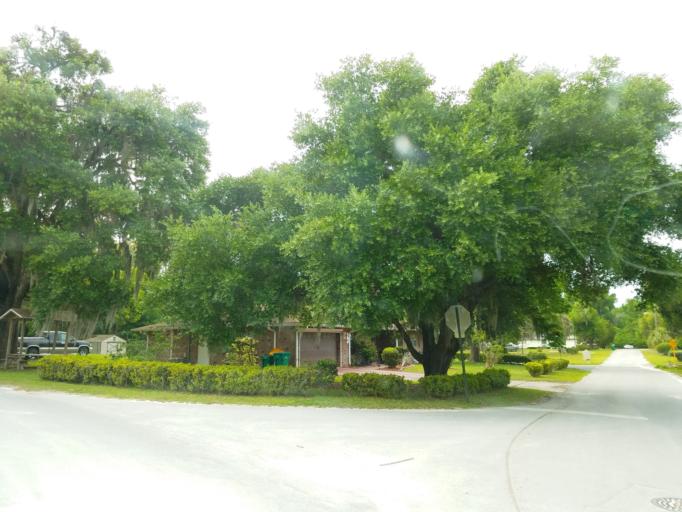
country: US
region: Florida
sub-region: Citrus County
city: Inverness
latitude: 28.8400
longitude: -82.3328
